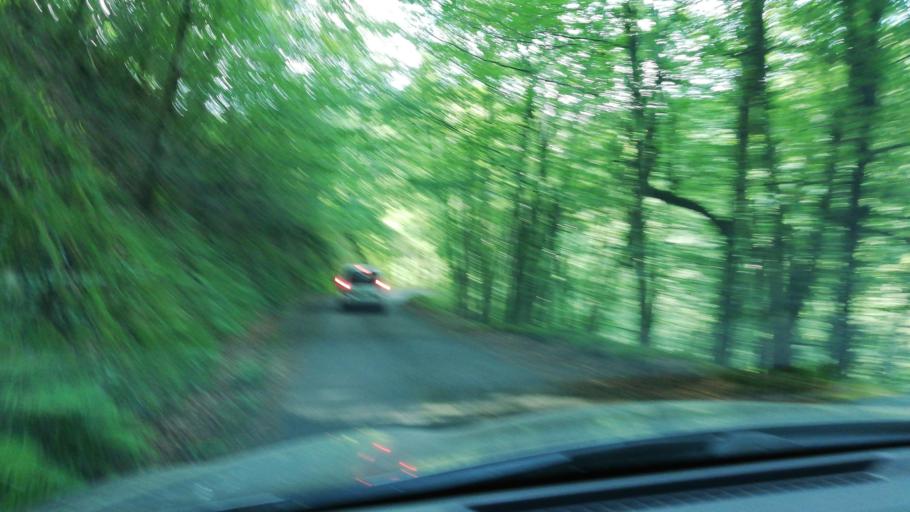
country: FR
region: Limousin
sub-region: Departement de la Correze
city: Argentat
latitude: 44.9794
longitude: 2.0281
